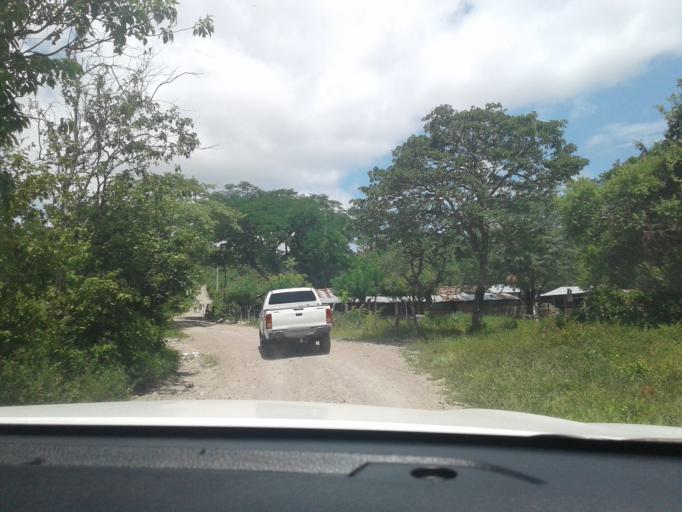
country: NI
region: Matagalpa
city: Terrabona
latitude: 12.5551
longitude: -86.0308
